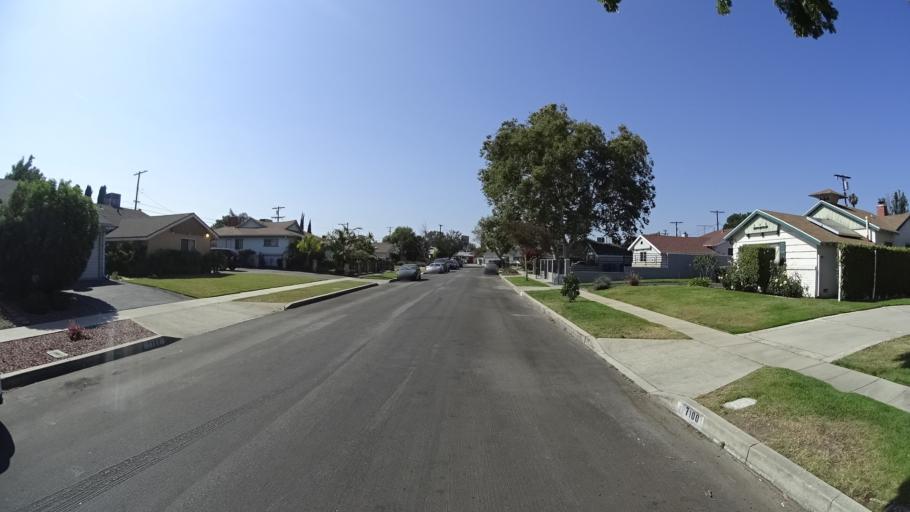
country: US
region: California
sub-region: Los Angeles County
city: Van Nuys
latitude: 34.1993
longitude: -118.4252
